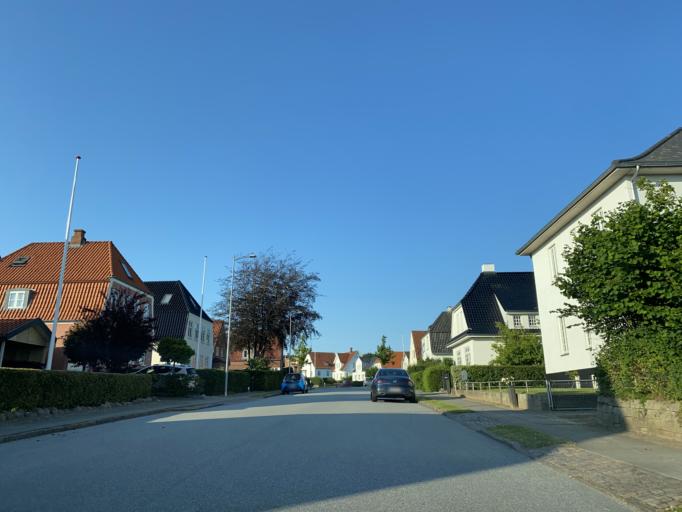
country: DK
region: South Denmark
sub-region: Aabenraa Kommune
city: Aabenraa
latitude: 55.0529
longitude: 9.4293
